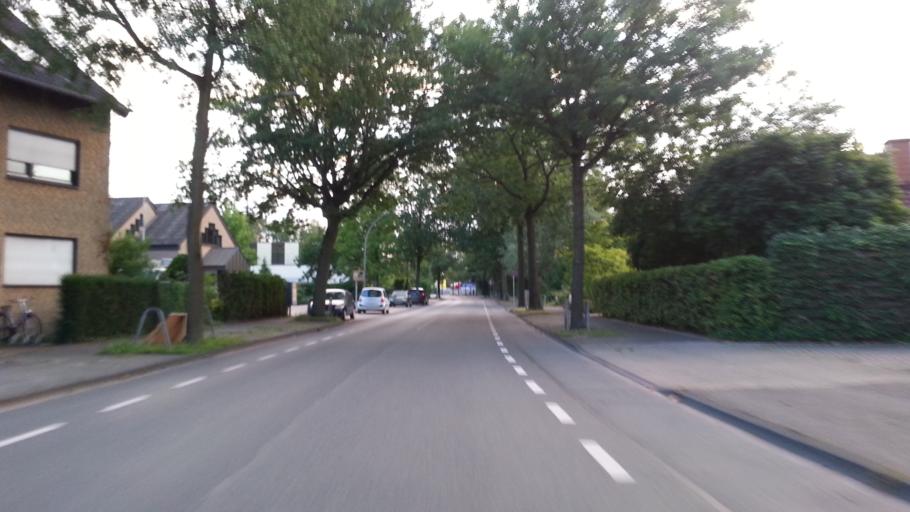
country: DE
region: North Rhine-Westphalia
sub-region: Regierungsbezirk Munster
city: Muenster
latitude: 51.9474
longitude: 7.5373
